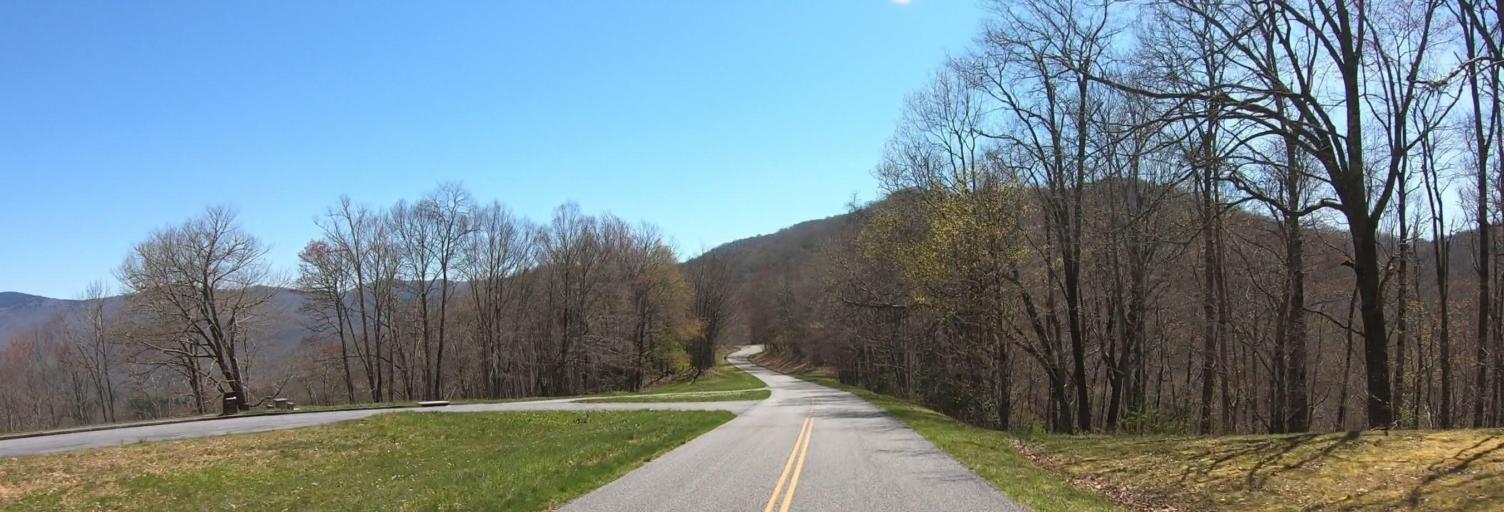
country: US
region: North Carolina
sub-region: Swain County
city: Cherokee
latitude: 35.5247
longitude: -83.2220
